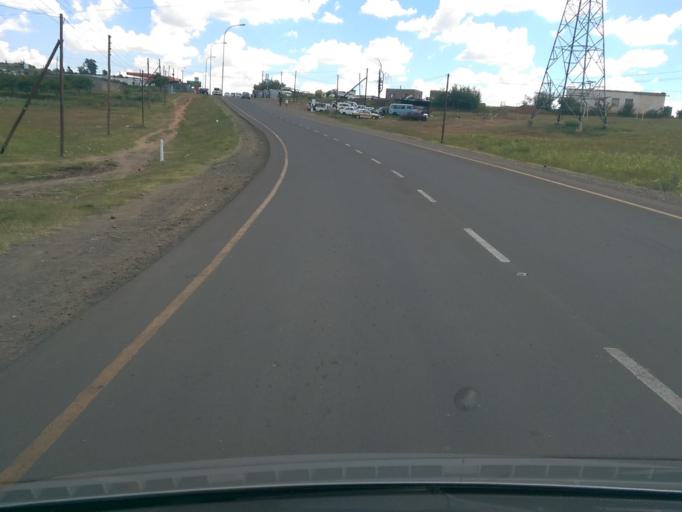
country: LS
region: Maseru
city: Maseru
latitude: -29.4033
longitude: 27.5642
